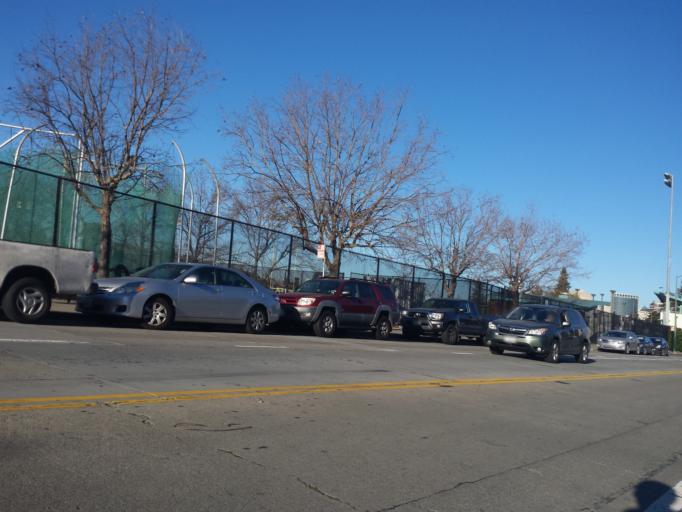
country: US
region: California
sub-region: Alameda County
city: Oakland
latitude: 37.7939
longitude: -122.2568
